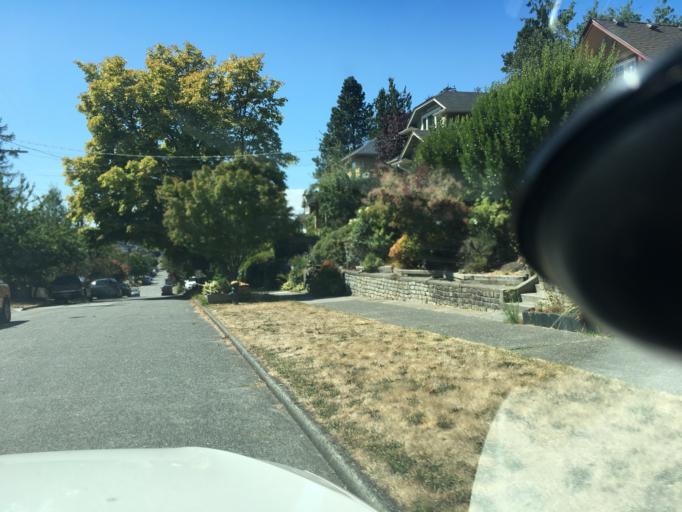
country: US
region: Washington
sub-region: King County
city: Shoreline
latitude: 47.6891
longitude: -122.3590
